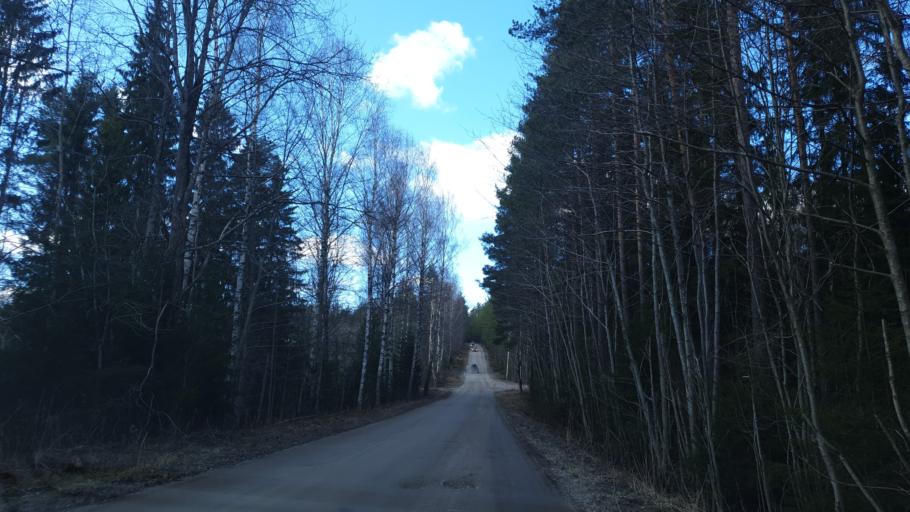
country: SE
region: OErebro
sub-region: Orebro Kommun
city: Garphyttan
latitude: 59.3515
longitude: 14.9875
